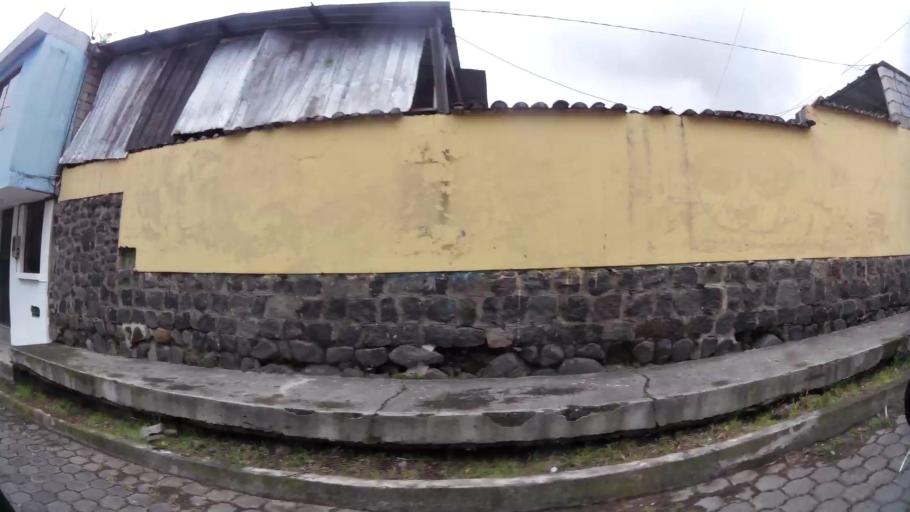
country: EC
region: Pichincha
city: Sangolqui
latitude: -0.3131
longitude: -78.4595
